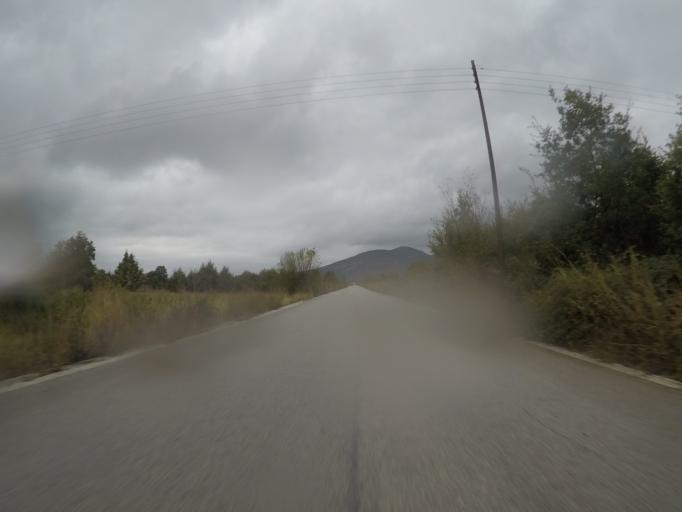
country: GR
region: Peloponnese
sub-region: Nomos Arkadias
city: Tripoli
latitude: 37.5859
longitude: 22.4254
